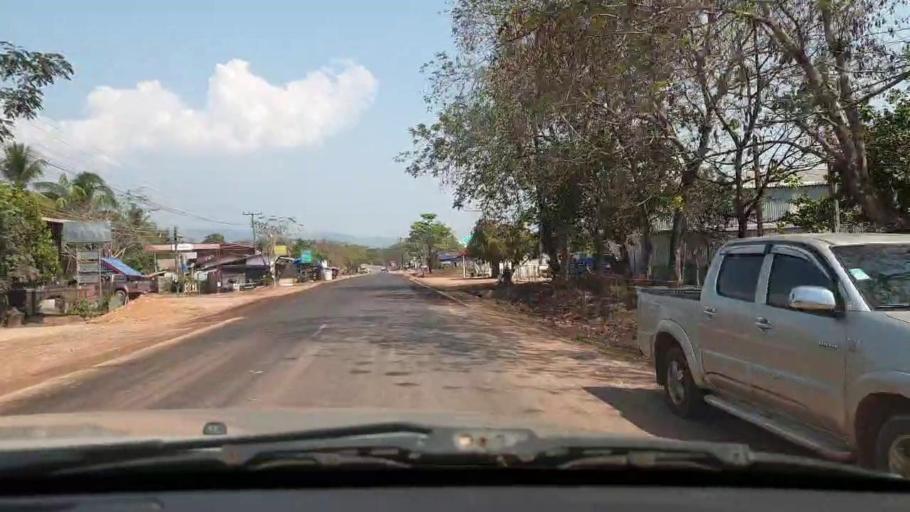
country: TH
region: Nong Khai
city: Rattanawapi
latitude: 18.1727
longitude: 103.0565
